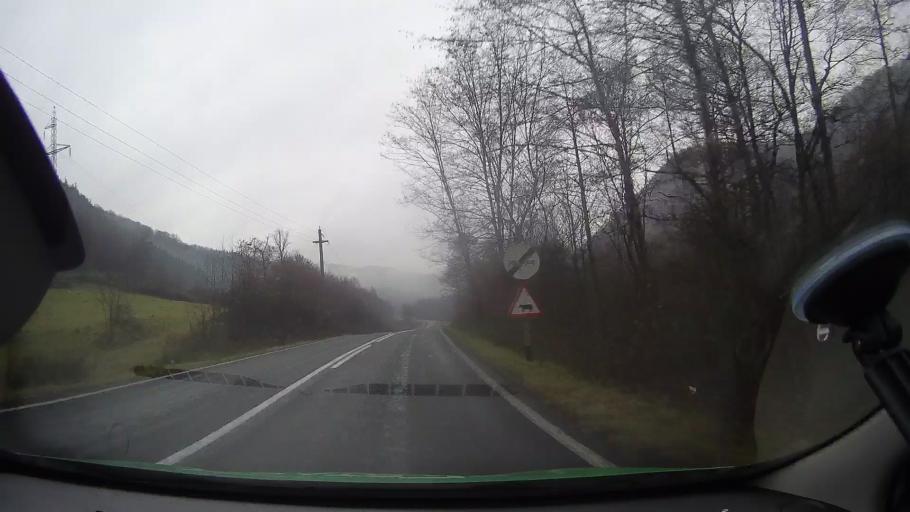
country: RO
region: Arad
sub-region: Comuna Plescuta
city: Plescuta
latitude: 46.3107
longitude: 22.4560
